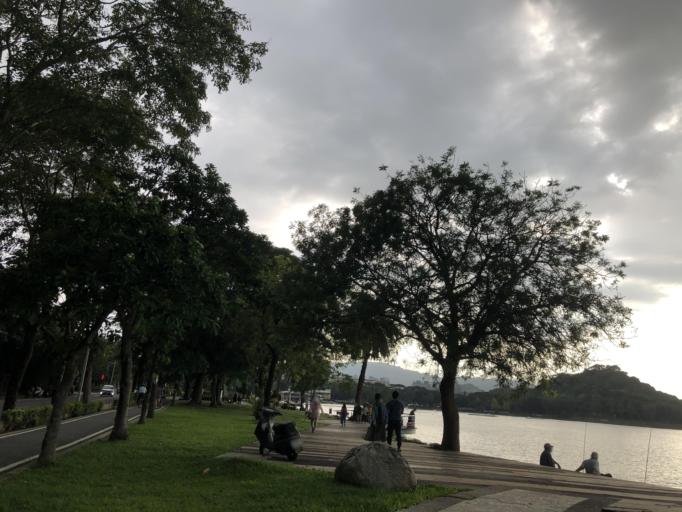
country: TW
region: Kaohsiung
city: Kaohsiung
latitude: 22.6817
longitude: 120.2978
